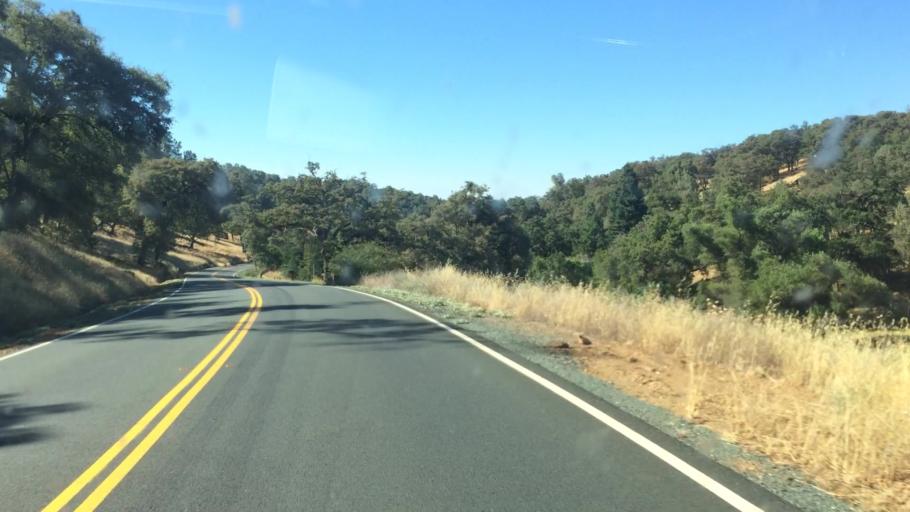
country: US
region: California
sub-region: El Dorado County
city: Deer Park
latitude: 38.6238
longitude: -120.8532
